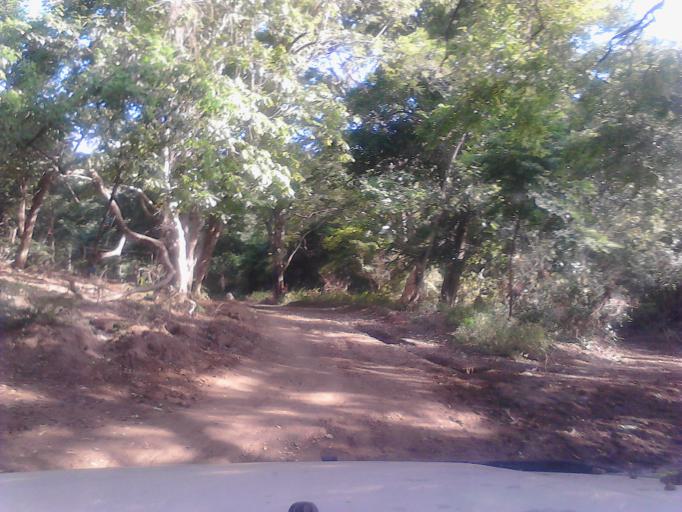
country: NI
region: Rivas
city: Tola
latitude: 11.4984
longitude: -86.0493
